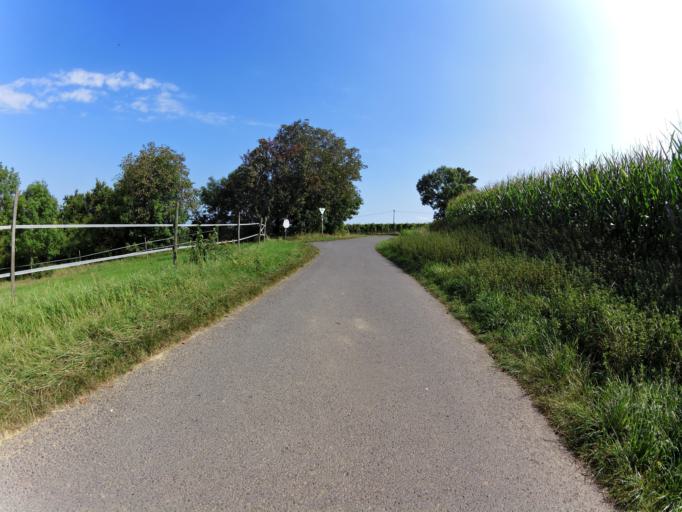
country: DE
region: Bavaria
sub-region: Regierungsbezirk Unterfranken
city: Sommerach
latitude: 49.8322
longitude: 10.1737
